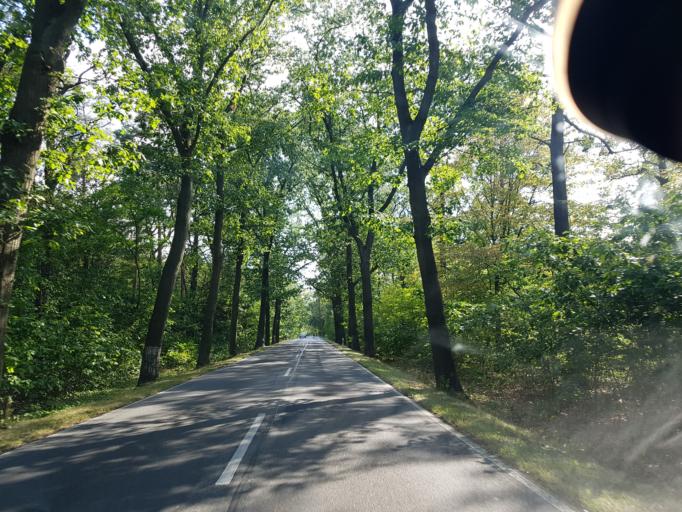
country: DE
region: Brandenburg
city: Calau
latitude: 51.7713
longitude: 13.9512
